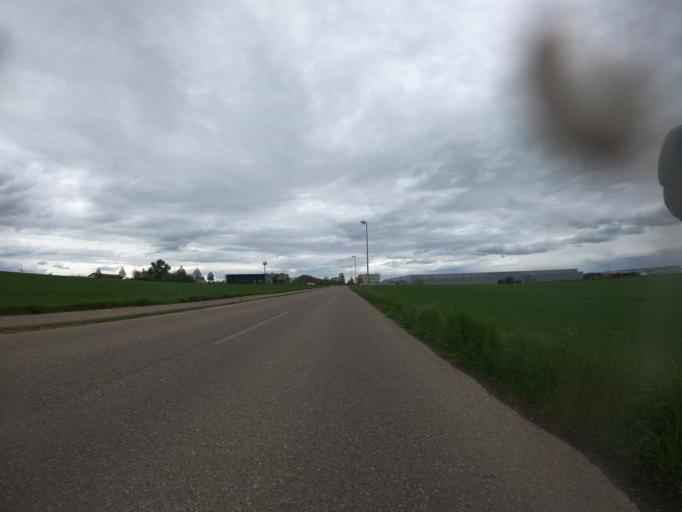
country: DE
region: Baden-Wuerttemberg
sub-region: Karlsruhe Region
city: Nagold
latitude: 48.5362
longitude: 8.7427
